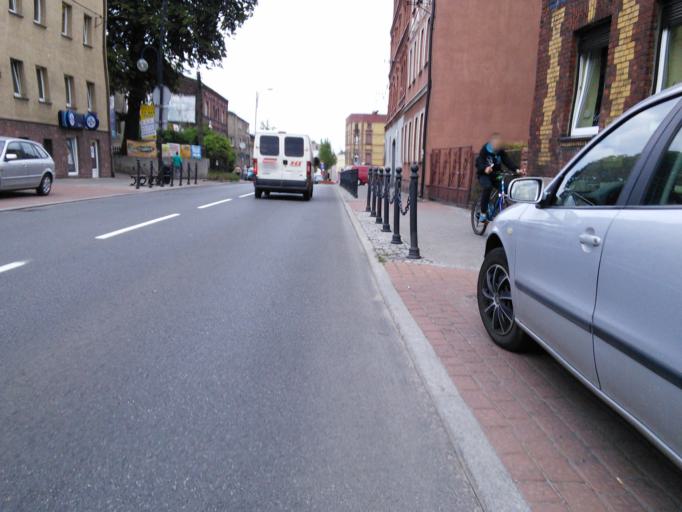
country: PL
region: Silesian Voivodeship
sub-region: Piekary Slaskie
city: Piekary Slaskie
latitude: 50.3859
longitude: 18.9444
